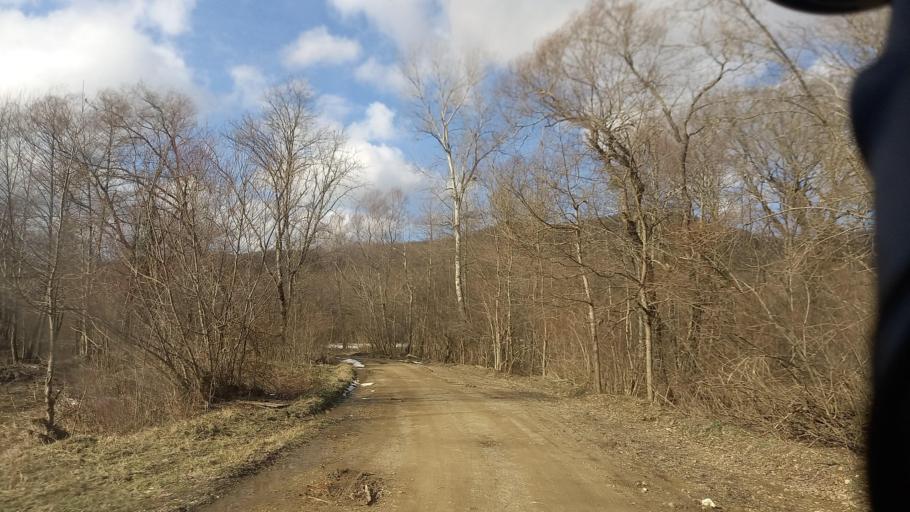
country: RU
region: Krasnodarskiy
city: Smolenskaya
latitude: 44.5992
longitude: 38.8797
